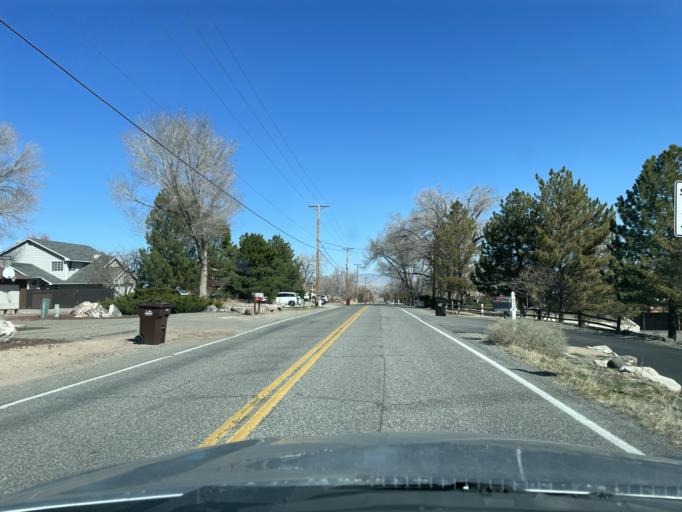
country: US
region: Colorado
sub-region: Mesa County
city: Redlands
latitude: 39.0794
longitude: -108.6688
